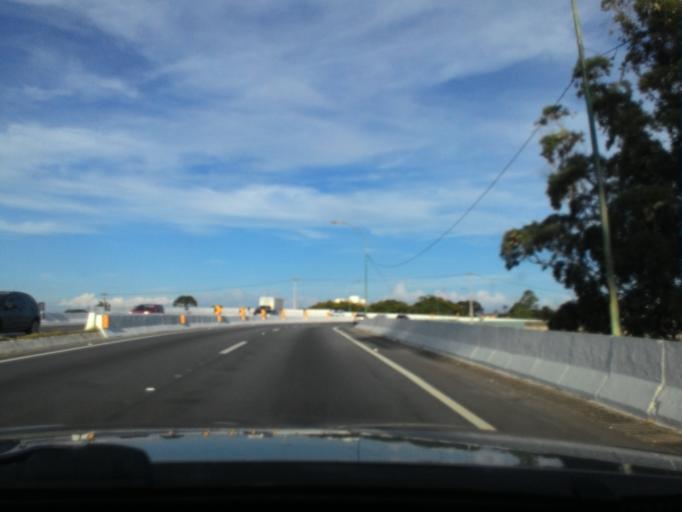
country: BR
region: Parana
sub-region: Curitiba
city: Curitiba
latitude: -25.4438
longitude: -49.2347
